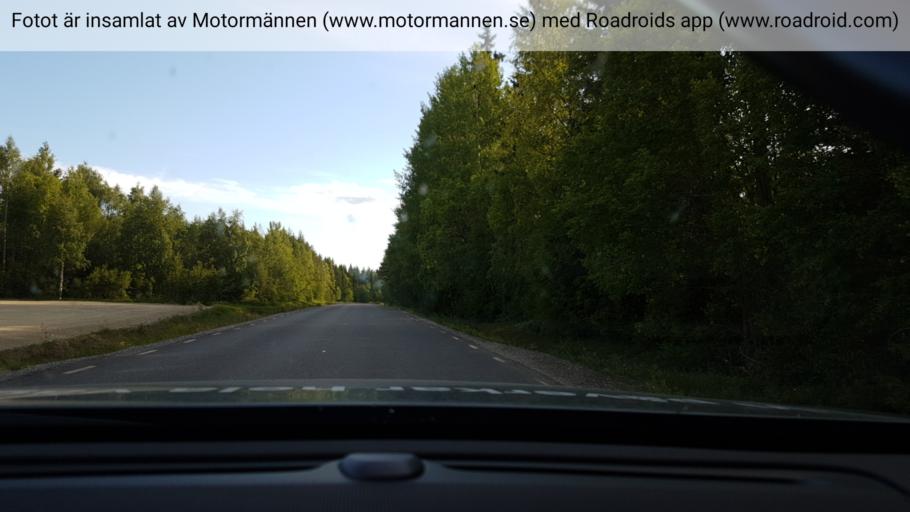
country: SE
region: Vaesterbotten
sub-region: Vannas Kommun
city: Vannasby
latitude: 64.0799
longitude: 19.9449
